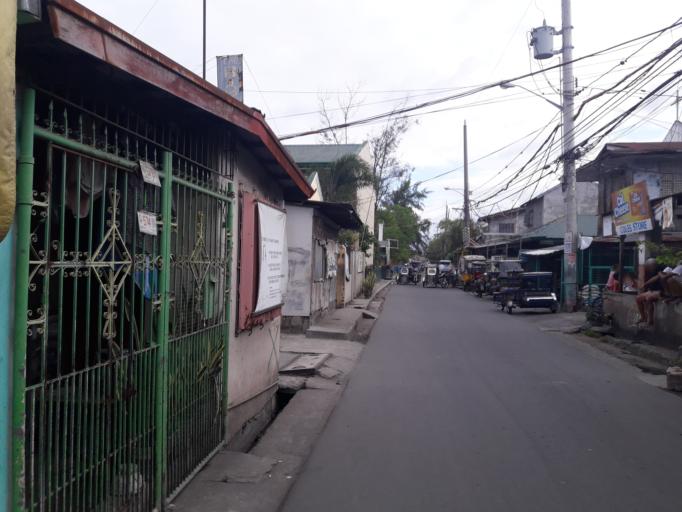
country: PH
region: Calabarzon
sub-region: Province of Laguna
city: Santa Rosa
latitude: 14.3049
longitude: 121.1248
